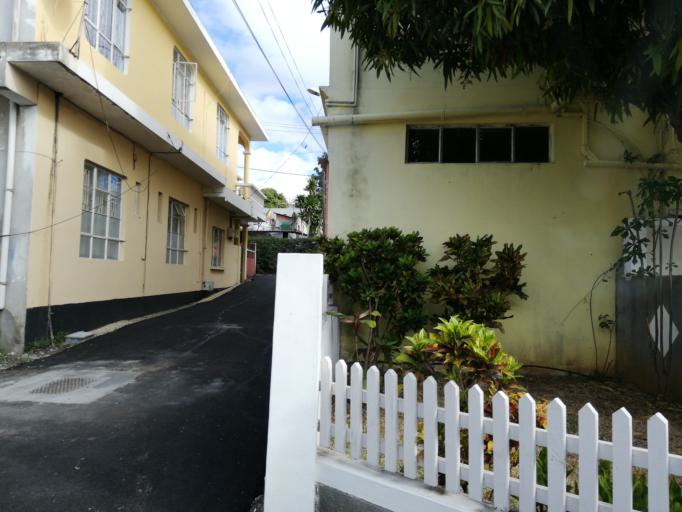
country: MU
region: Black River
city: Gros Cailloux
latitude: -20.2310
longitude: 57.4562
